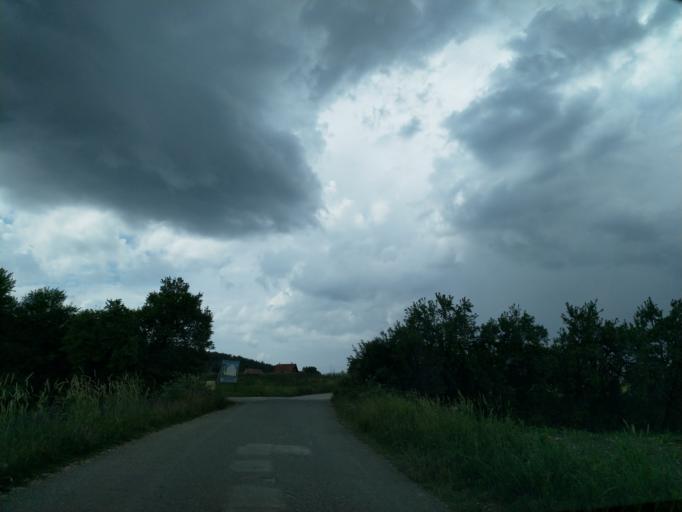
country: RS
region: Central Serbia
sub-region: Borski Okrug
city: Bor
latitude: 44.0289
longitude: 21.9671
